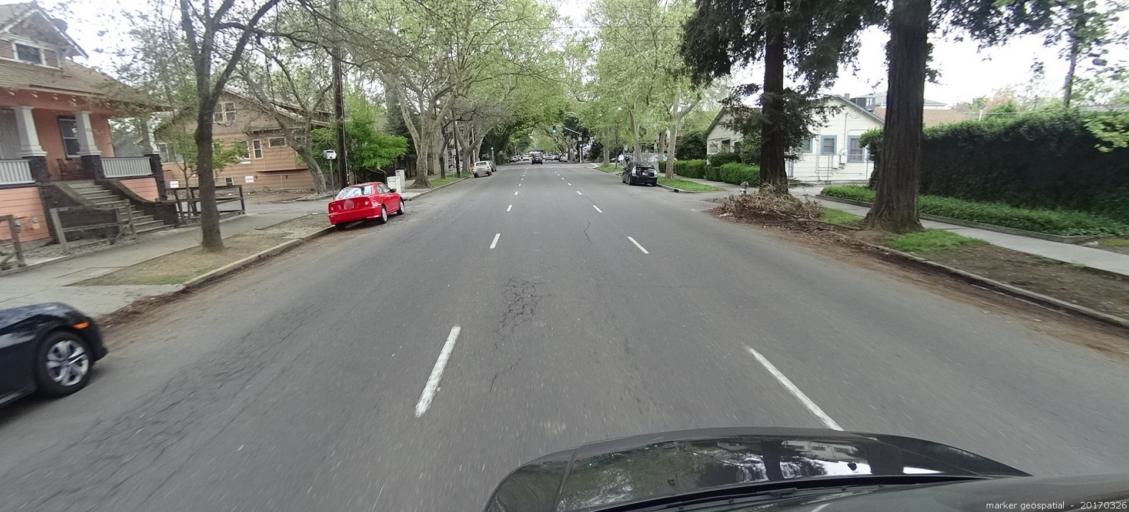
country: US
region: California
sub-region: Sacramento County
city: Sacramento
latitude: 38.5683
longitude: -121.4910
